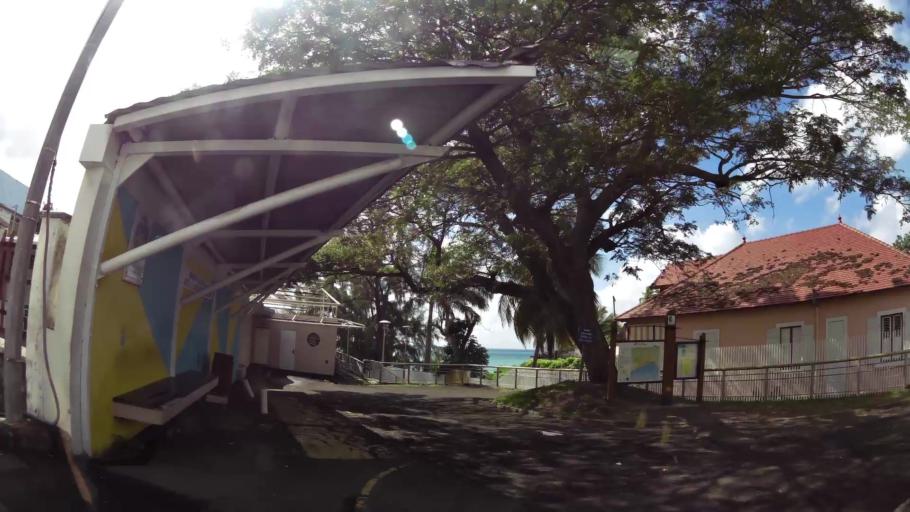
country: MQ
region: Martinique
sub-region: Martinique
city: Les Trois-Ilets
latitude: 14.4810
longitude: -61.0221
